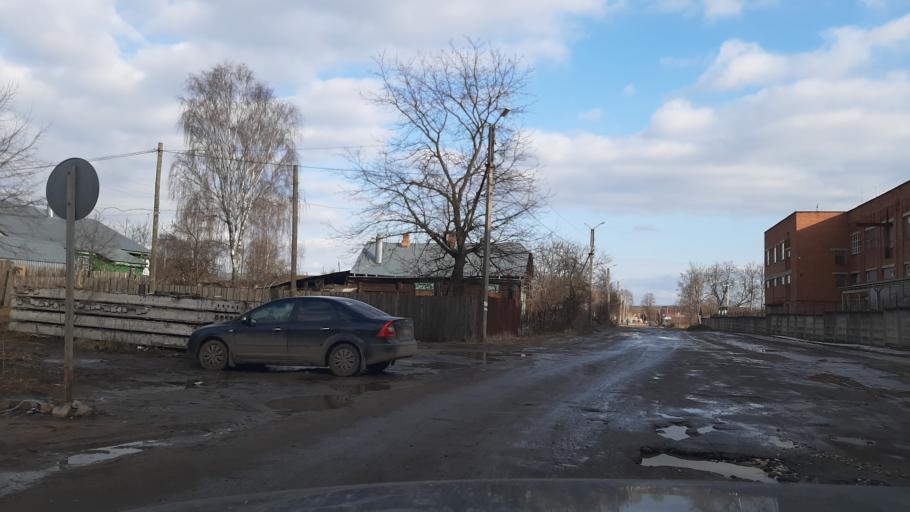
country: RU
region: Ivanovo
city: Teykovo
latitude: 56.8532
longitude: 40.5545
